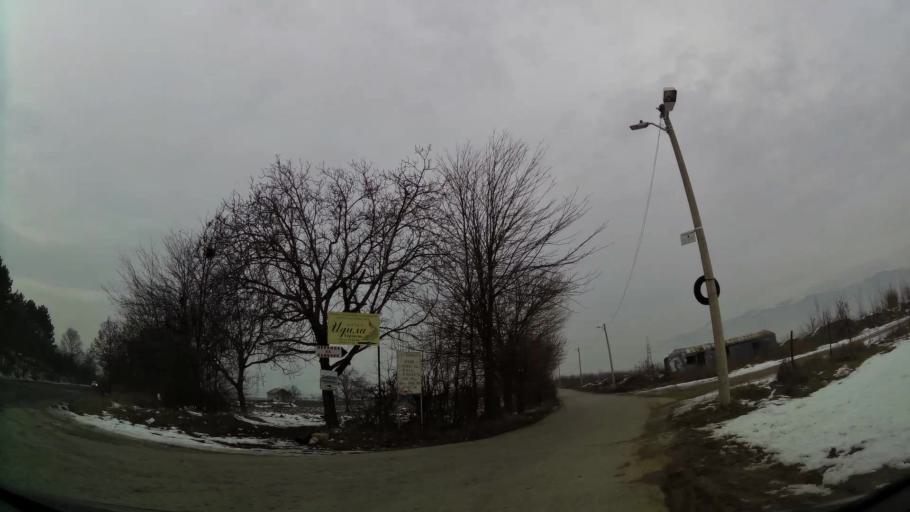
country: MK
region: Suto Orizari
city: Suto Orizare
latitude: 42.0426
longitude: 21.4373
